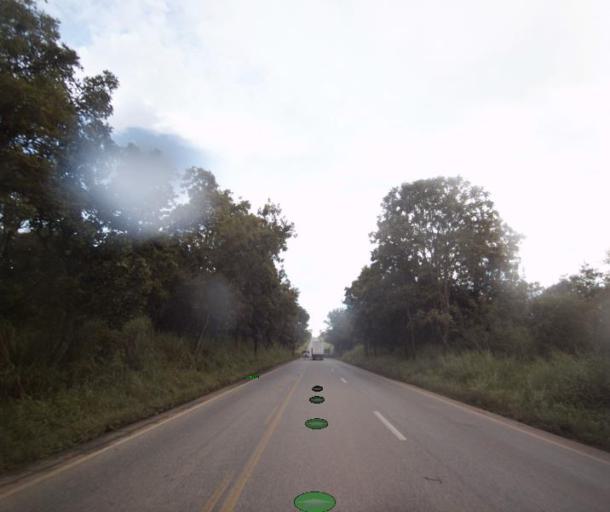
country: BR
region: Goias
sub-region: Porangatu
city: Porangatu
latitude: -13.9734
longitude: -49.0904
